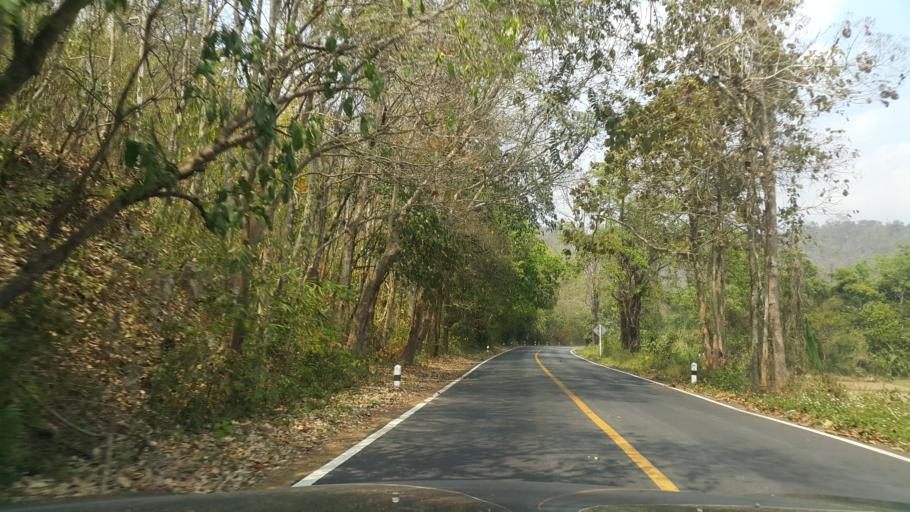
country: TH
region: Lamphun
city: Thung Hua Chang
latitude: 17.9039
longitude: 99.1146
